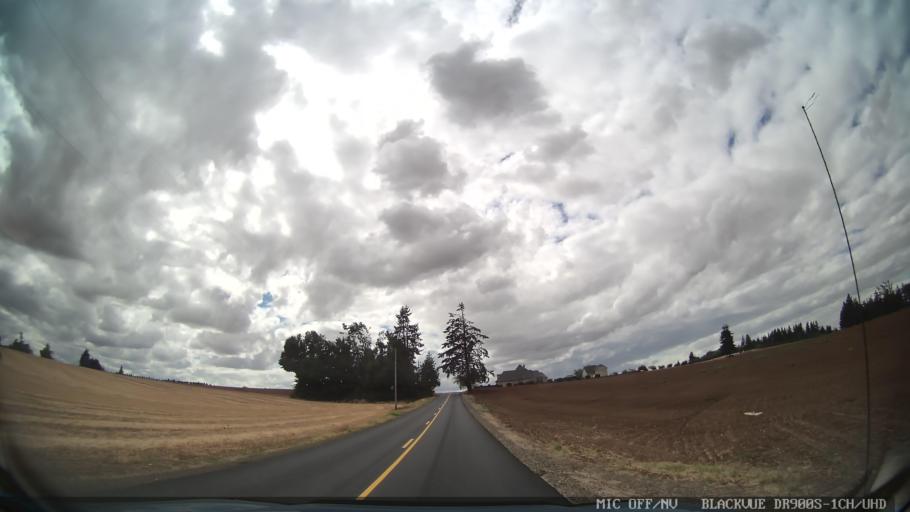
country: US
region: Oregon
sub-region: Marion County
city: Sublimity
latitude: 44.8405
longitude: -122.7858
